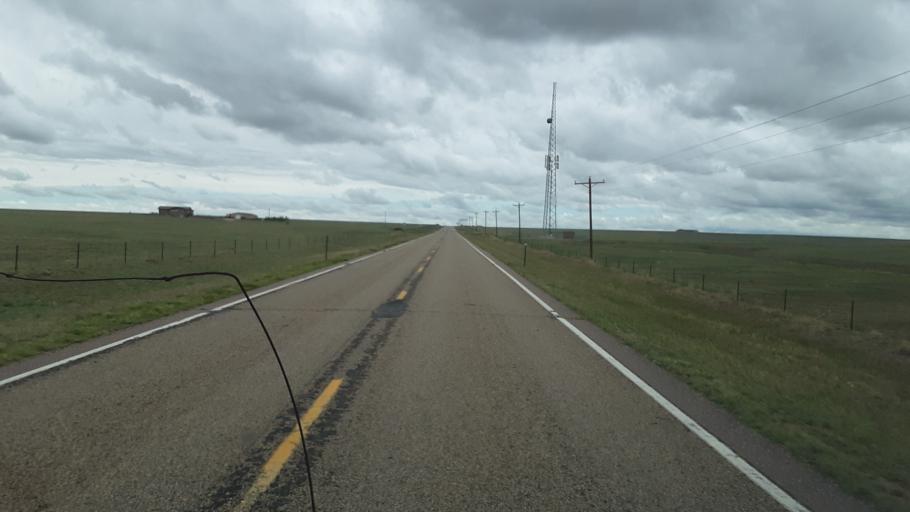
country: US
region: Colorado
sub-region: El Paso County
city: Ellicott
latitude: 38.8399
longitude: -104.0133
